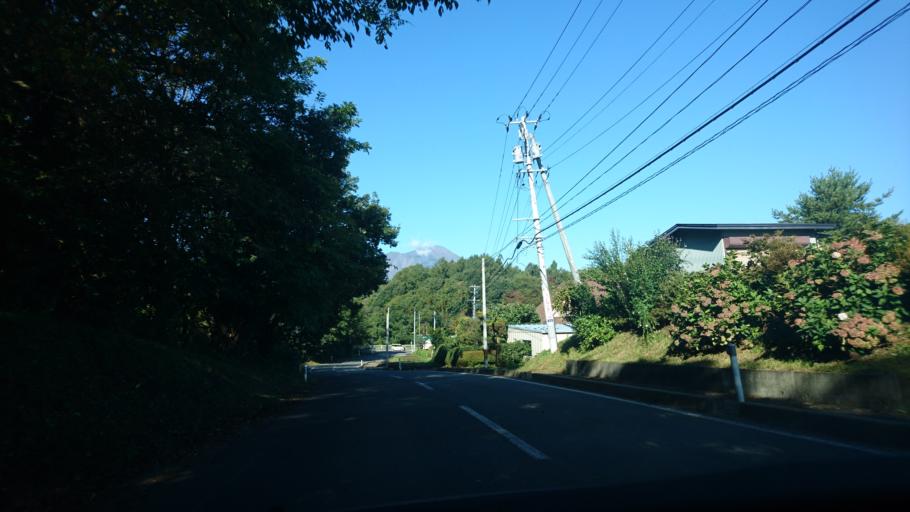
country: JP
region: Iwate
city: Morioka-shi
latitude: 39.8115
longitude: 141.1320
